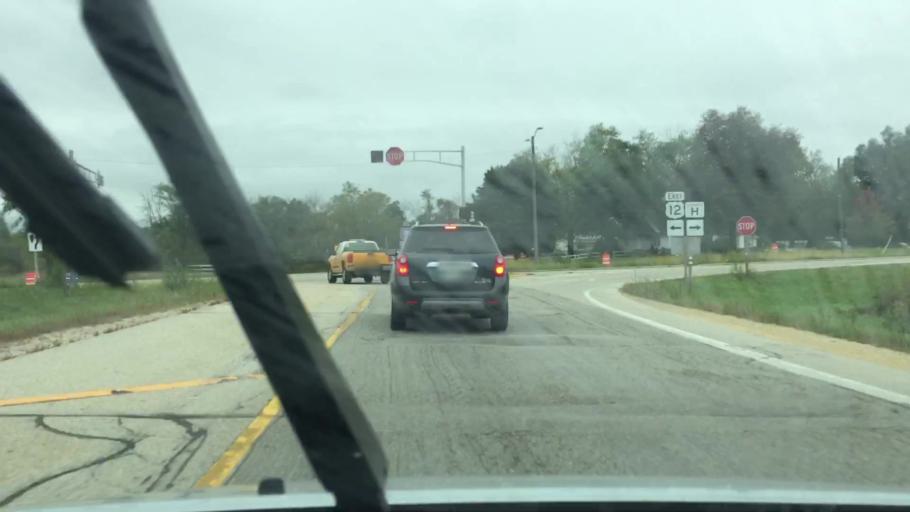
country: US
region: Wisconsin
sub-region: Walworth County
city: Genoa City
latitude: 42.4989
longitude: -88.3180
